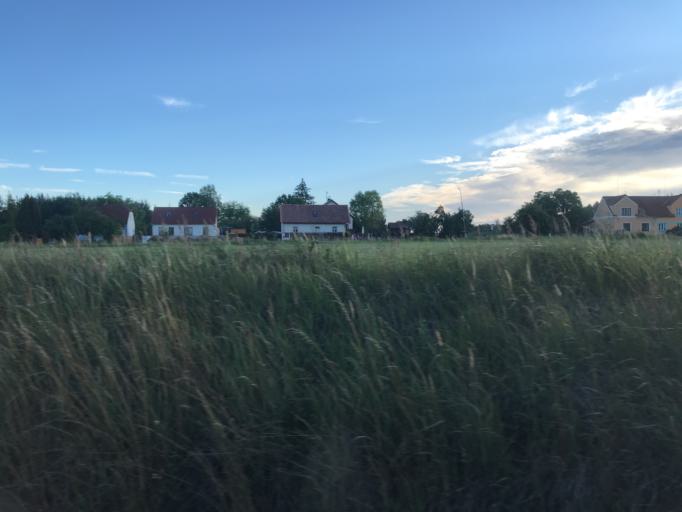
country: CZ
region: Jihocesky
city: Suchdol nad Luznici
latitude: 48.8577
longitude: 14.8943
